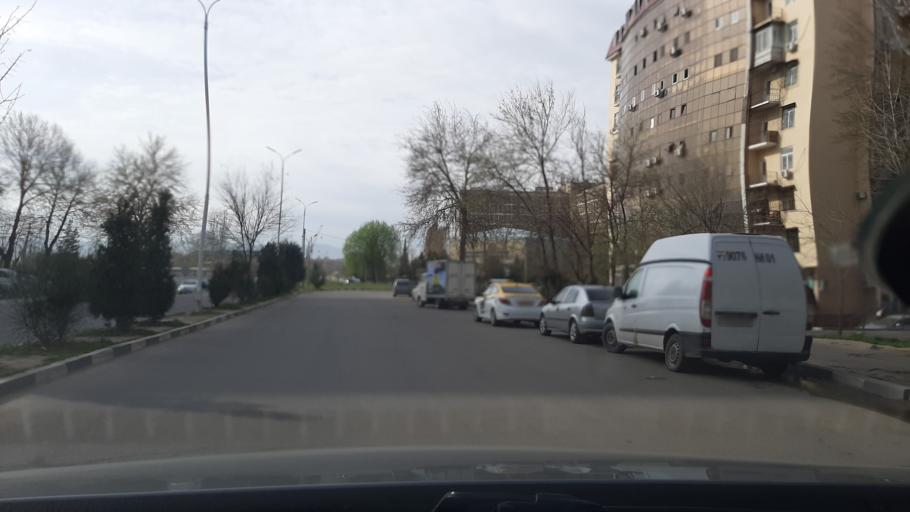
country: TJ
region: Dushanbe
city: Dushanbe
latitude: 38.5787
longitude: 68.7490
